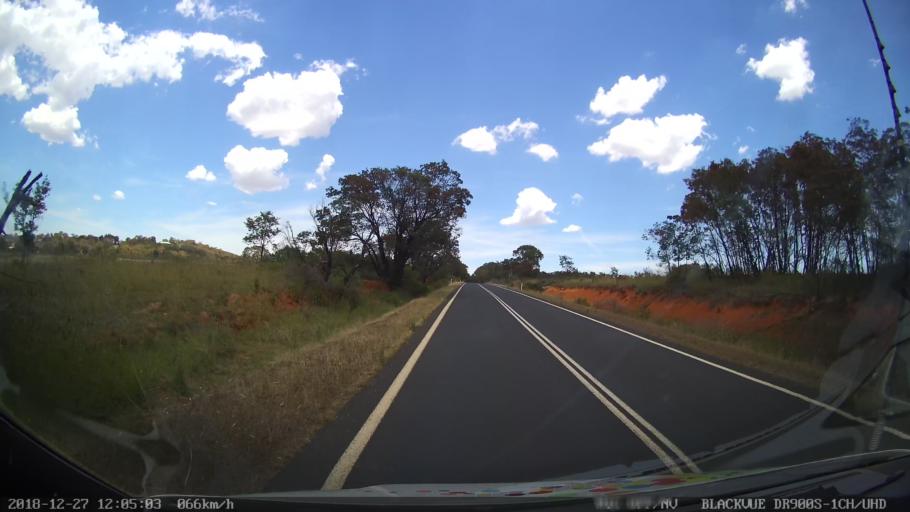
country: AU
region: New South Wales
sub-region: Blayney
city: Blayney
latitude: -33.8001
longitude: 149.3428
